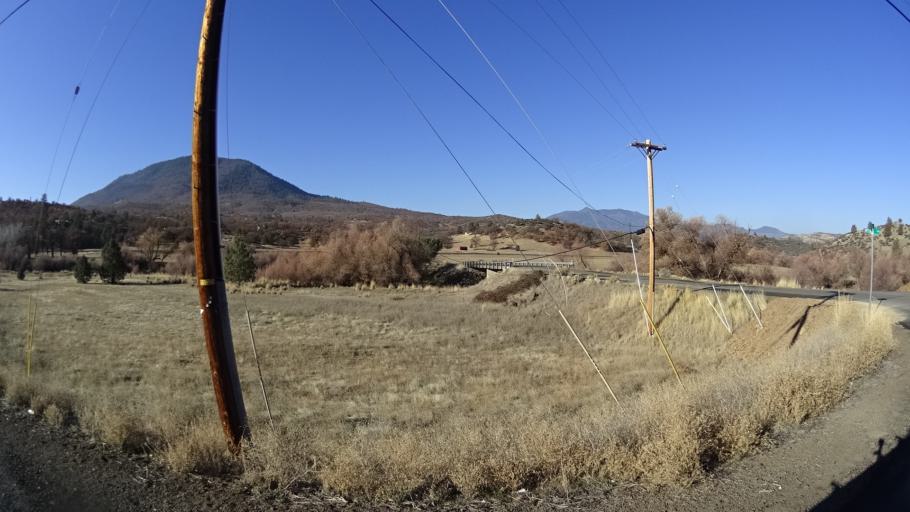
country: US
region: California
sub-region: Siskiyou County
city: Montague
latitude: 41.8904
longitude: -122.4808
